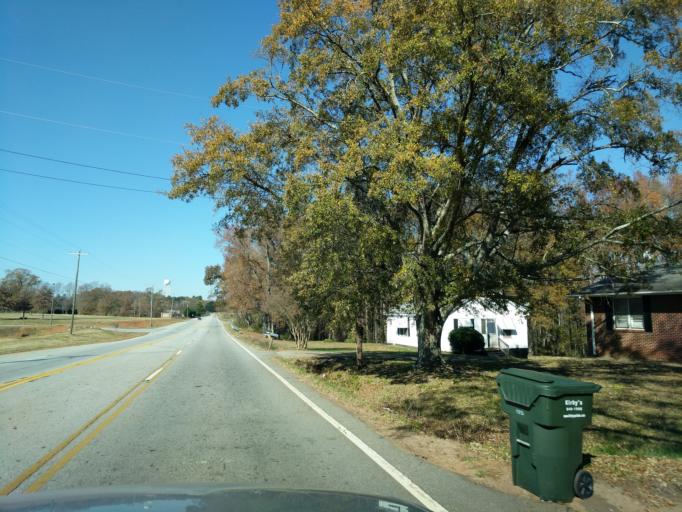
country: US
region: South Carolina
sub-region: Spartanburg County
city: Duncan
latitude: 34.9768
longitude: -82.1603
